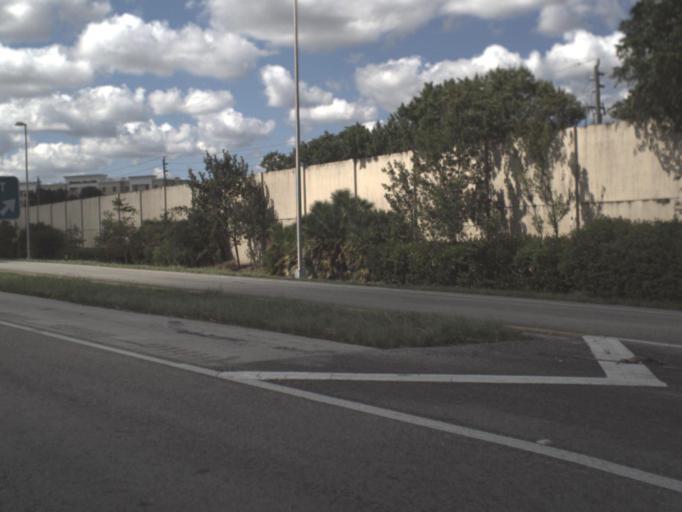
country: US
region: Florida
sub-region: Broward County
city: Parkland
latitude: 26.3003
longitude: -80.1971
